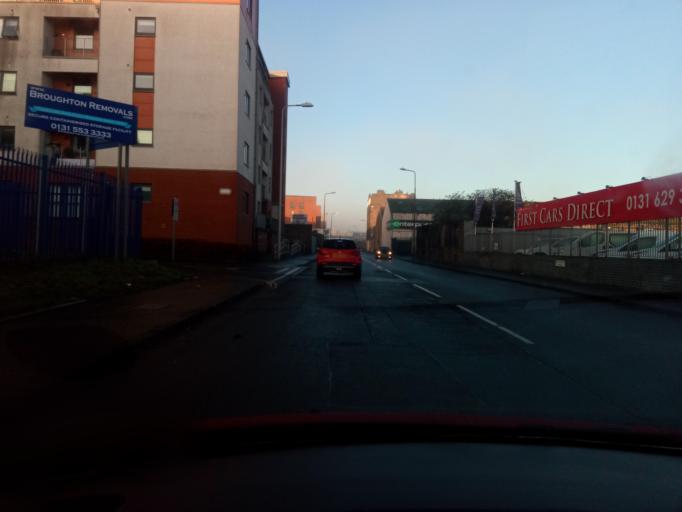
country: GB
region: Scotland
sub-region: West Lothian
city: Seafield
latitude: 55.9738
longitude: -3.1585
